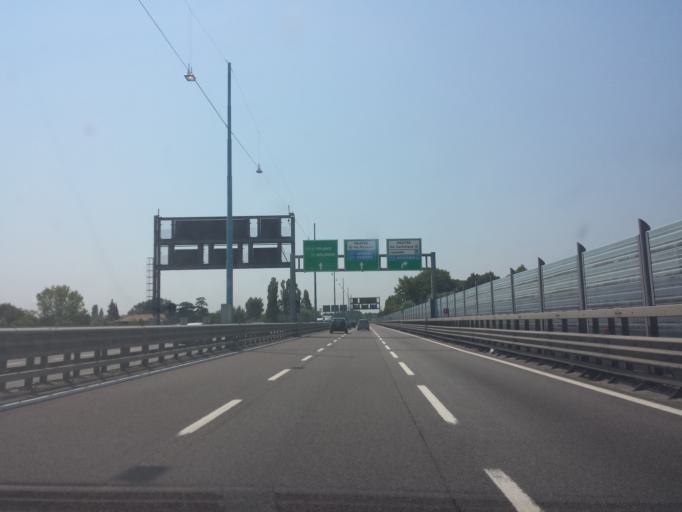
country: IT
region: Veneto
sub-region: Provincia di Venezia
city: Zelarino
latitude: 45.5138
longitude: 12.2418
